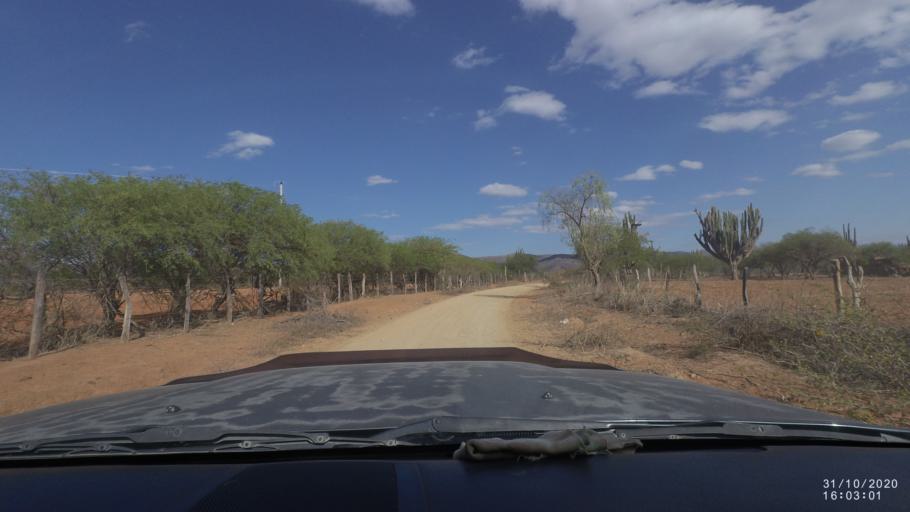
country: BO
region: Chuquisaca
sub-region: Provincia Zudanez
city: Mojocoya
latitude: -18.3491
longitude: -64.6546
